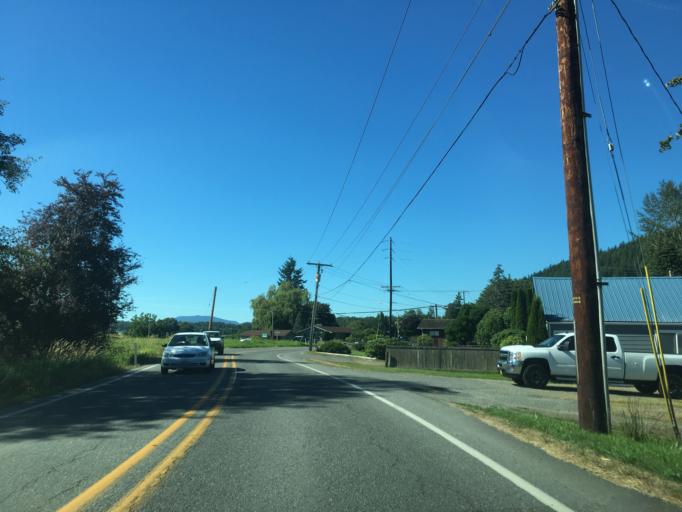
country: US
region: Washington
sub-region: Skagit County
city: Clear Lake
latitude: 48.4669
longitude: -122.2361
